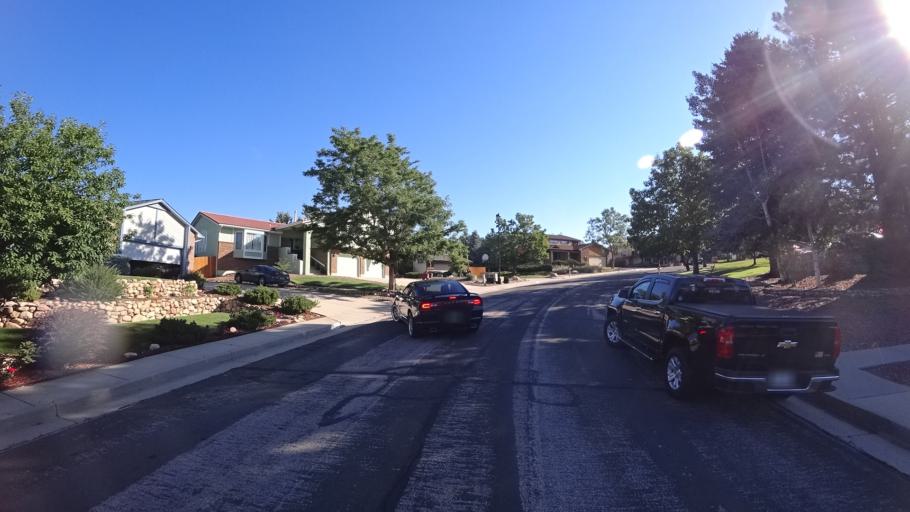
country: US
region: Colorado
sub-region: El Paso County
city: Black Forest
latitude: 38.9558
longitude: -104.7693
